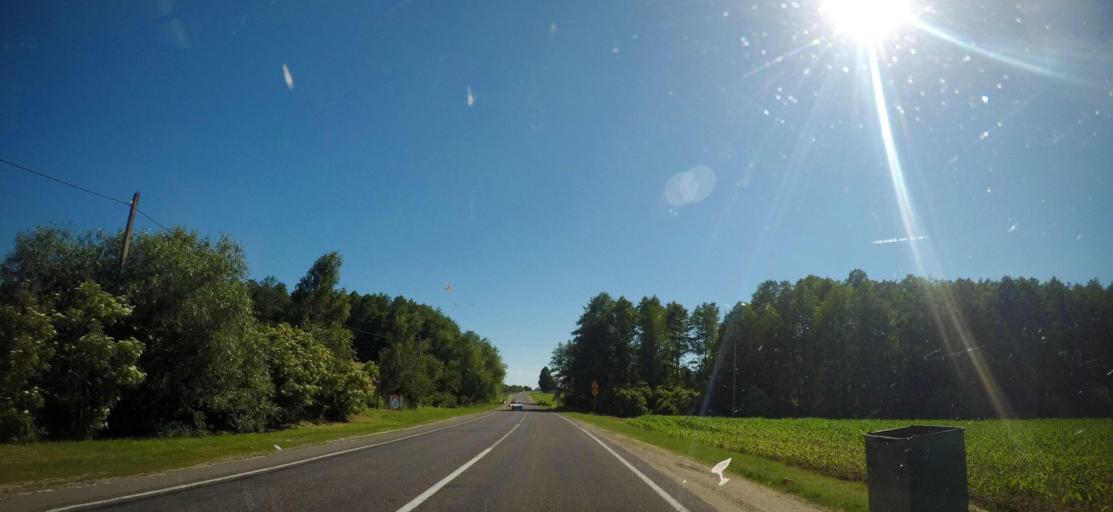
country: BY
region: Grodnenskaya
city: Vyalikaya Byerastavitsa
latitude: 53.1765
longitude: 23.9998
